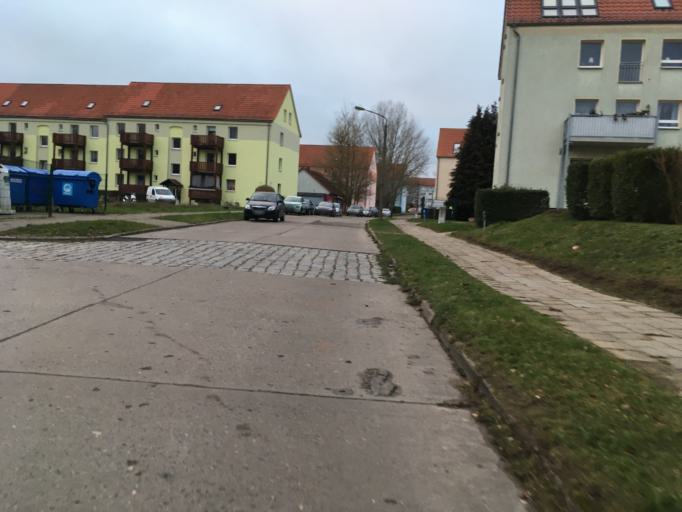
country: DE
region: Mecklenburg-Vorpommern
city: Sassnitz
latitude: 54.5101
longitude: 13.6263
